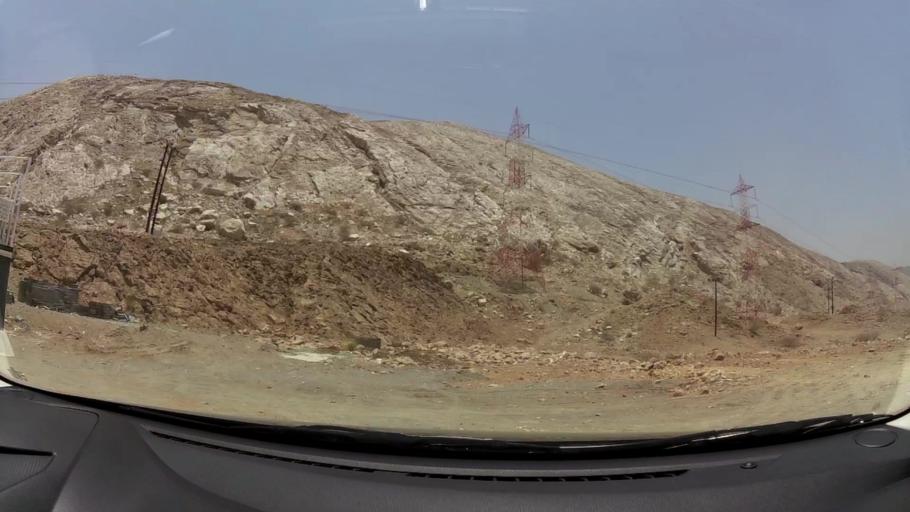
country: OM
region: Muhafazat Masqat
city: Bawshar
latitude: 23.5603
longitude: 58.4224
